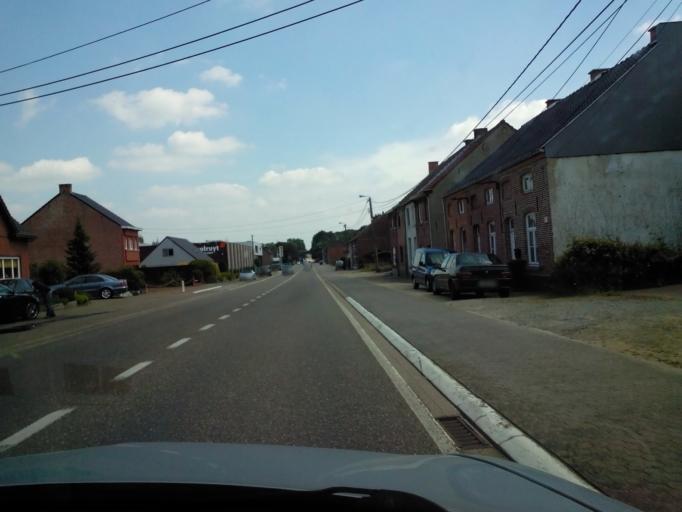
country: BE
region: Flanders
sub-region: Provincie Vlaams-Brabant
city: Aarschot
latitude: 50.9751
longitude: 4.8091
